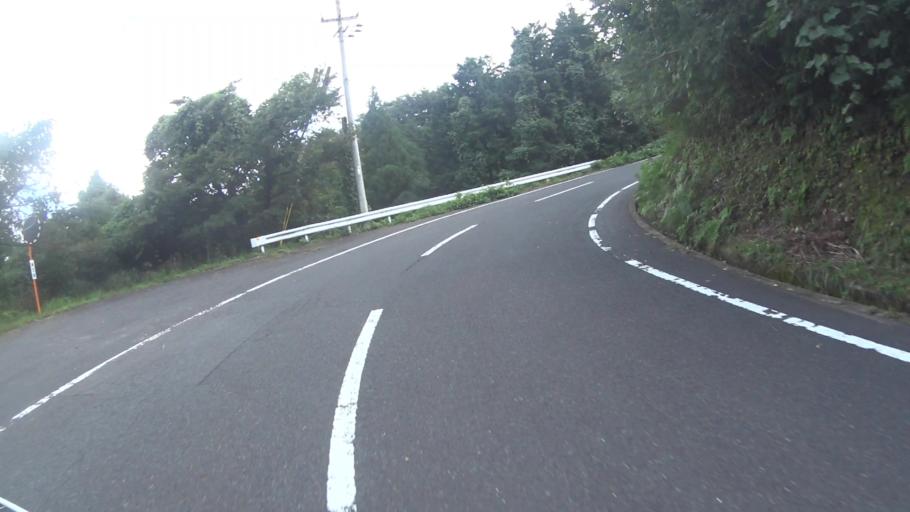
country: JP
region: Kyoto
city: Miyazu
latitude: 35.7336
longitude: 135.1796
